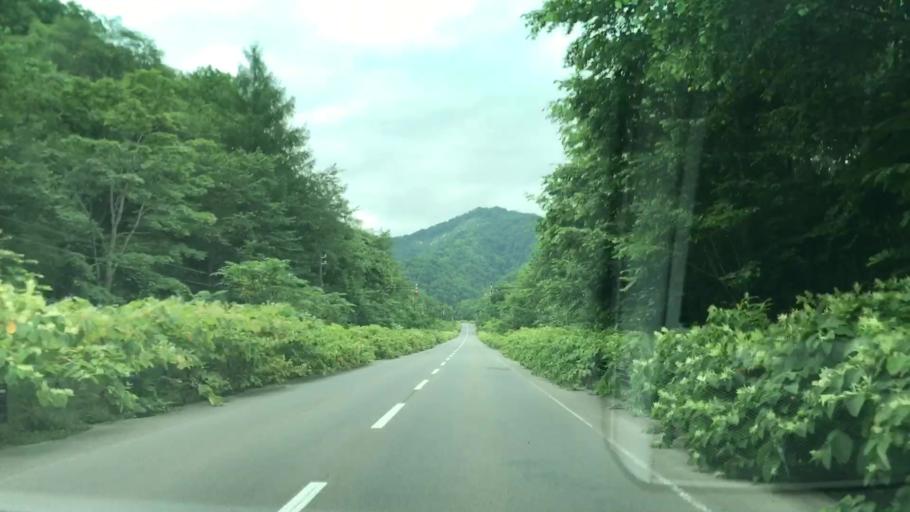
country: JP
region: Hokkaido
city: Yoichi
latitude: 43.0199
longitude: 140.8678
